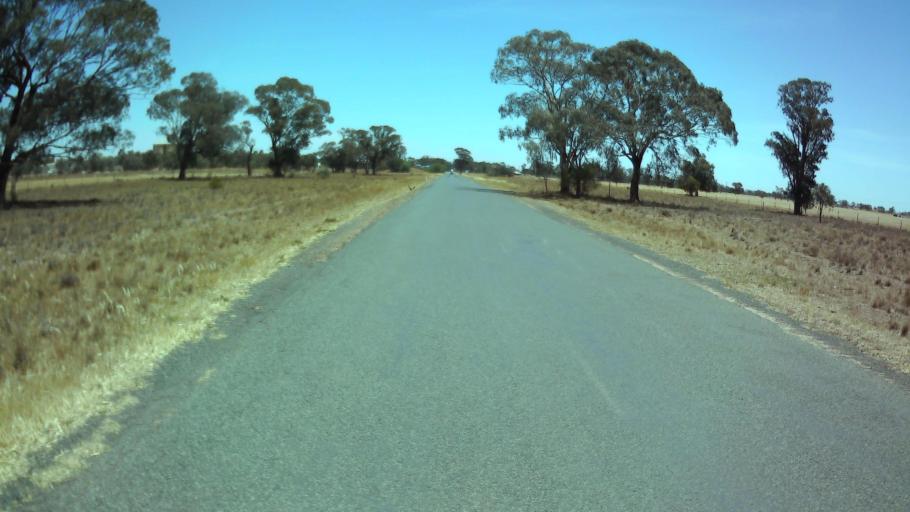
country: AU
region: New South Wales
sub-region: Weddin
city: Grenfell
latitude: -34.0111
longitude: 147.8036
